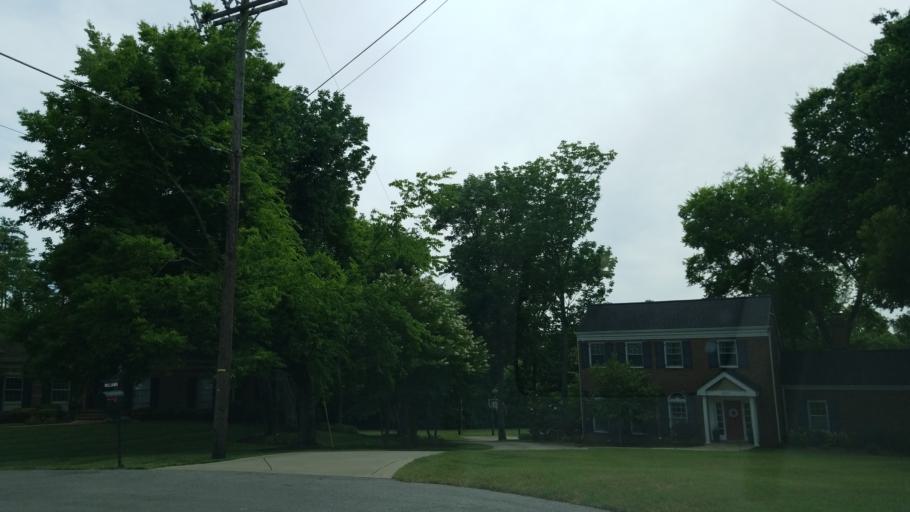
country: US
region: Tennessee
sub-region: Davidson County
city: Forest Hills
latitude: 36.0395
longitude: -86.8281
